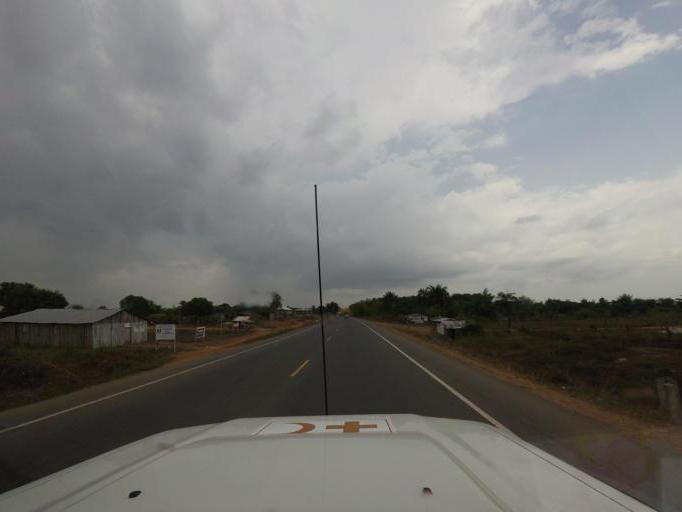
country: LR
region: Montserrado
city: Bensonville City
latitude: 6.3733
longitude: -10.6142
